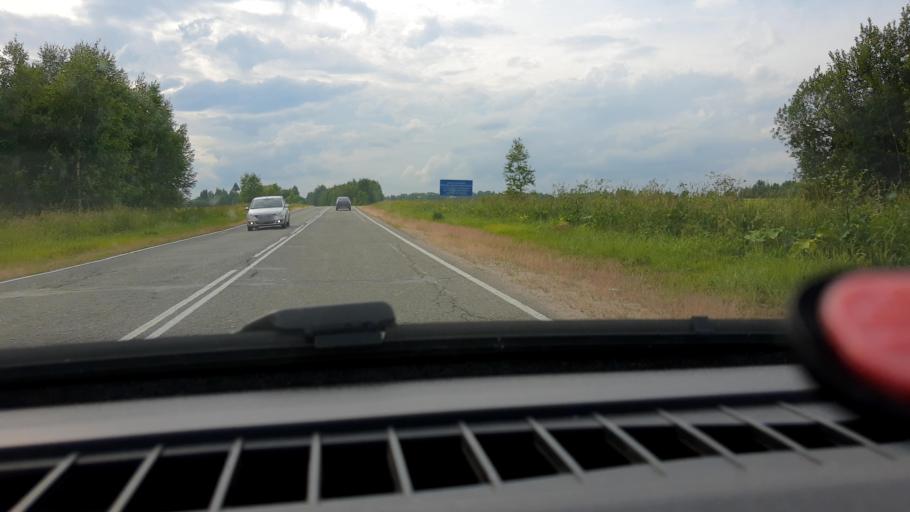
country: RU
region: Nizjnij Novgorod
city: Neklyudovo
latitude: 56.5059
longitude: 43.9741
